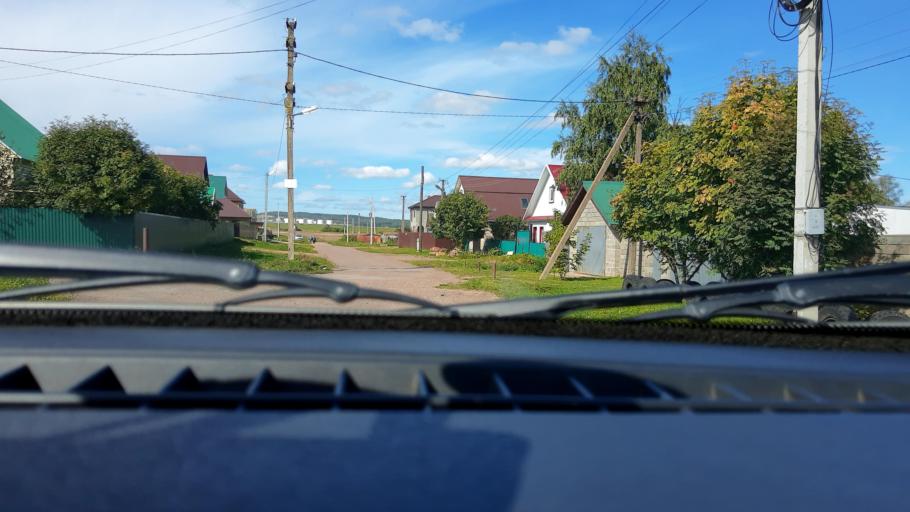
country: RU
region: Bashkortostan
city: Mikhaylovka
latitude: 54.8188
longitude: 55.7919
